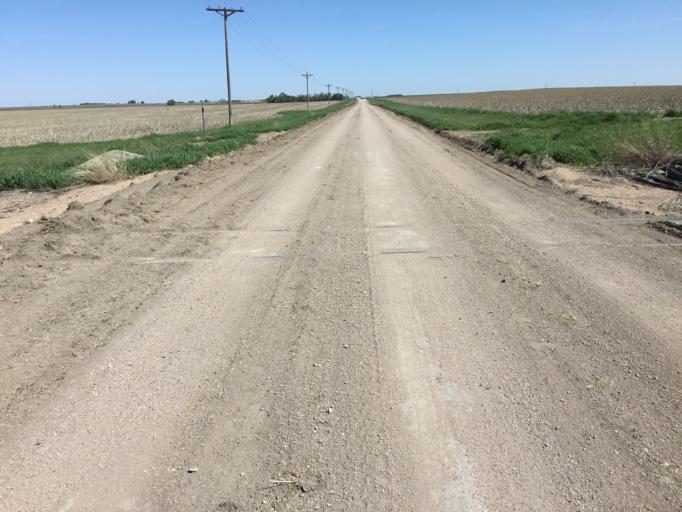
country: US
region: Kansas
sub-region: Smith County
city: Smith Center
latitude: 39.7633
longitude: -98.9356
